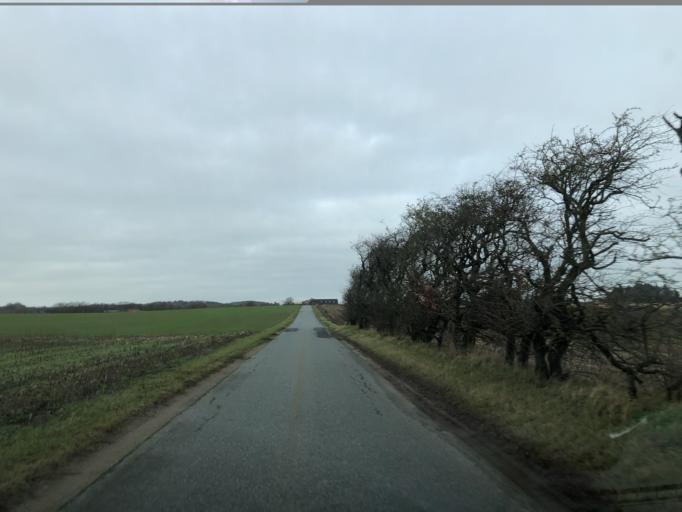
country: DK
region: Central Jutland
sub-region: Viborg Kommune
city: Stoholm
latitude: 56.4506
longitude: 9.1277
